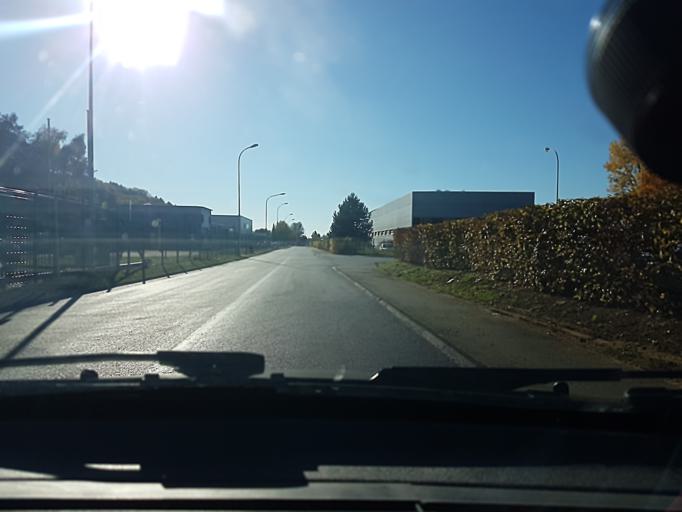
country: FR
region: Franche-Comte
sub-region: Departement du Doubs
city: Etupes
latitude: 47.5159
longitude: 6.8751
